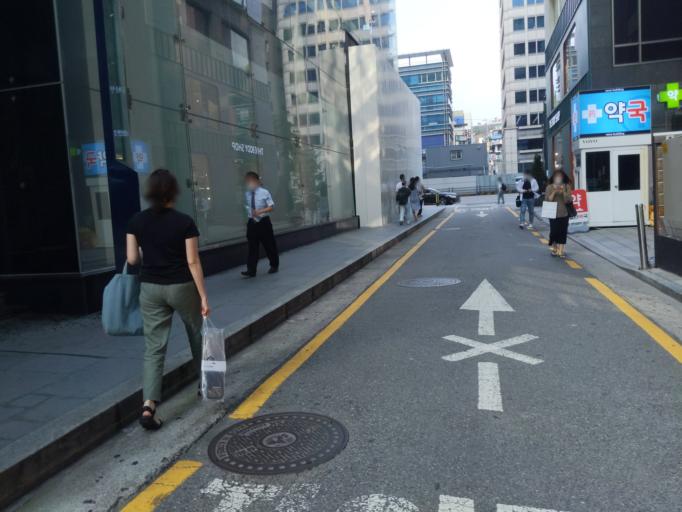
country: KR
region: Seoul
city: Seoul
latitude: 37.5023
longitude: 127.0249
